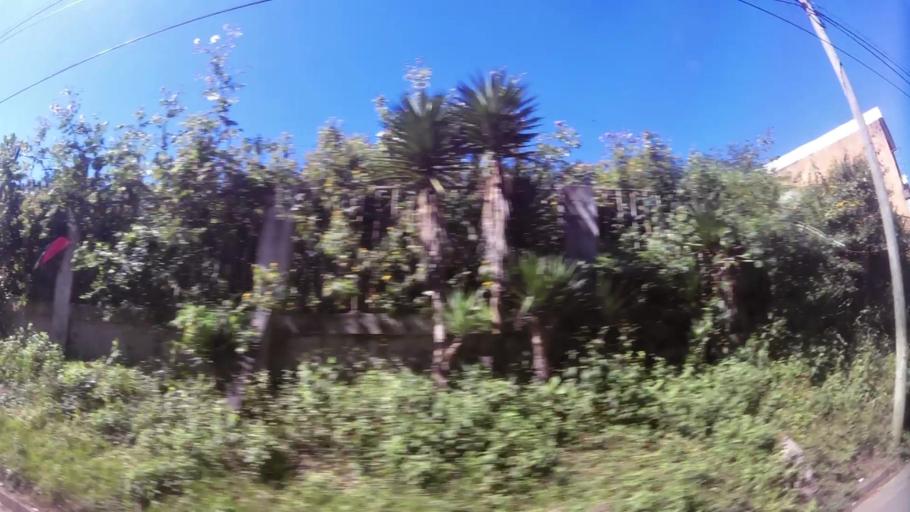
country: GT
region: Guatemala
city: San Jose Pinula
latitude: 14.5109
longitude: -90.4237
